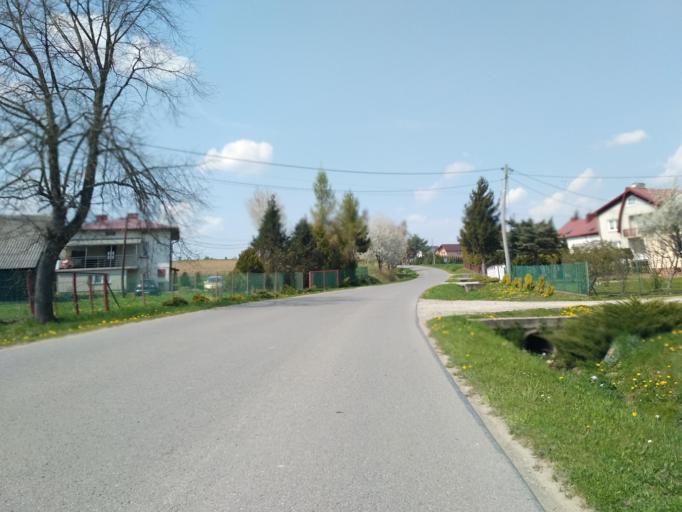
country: PL
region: Subcarpathian Voivodeship
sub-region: Powiat jasielski
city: Tarnowiec
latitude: 49.6698
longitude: 21.5579
